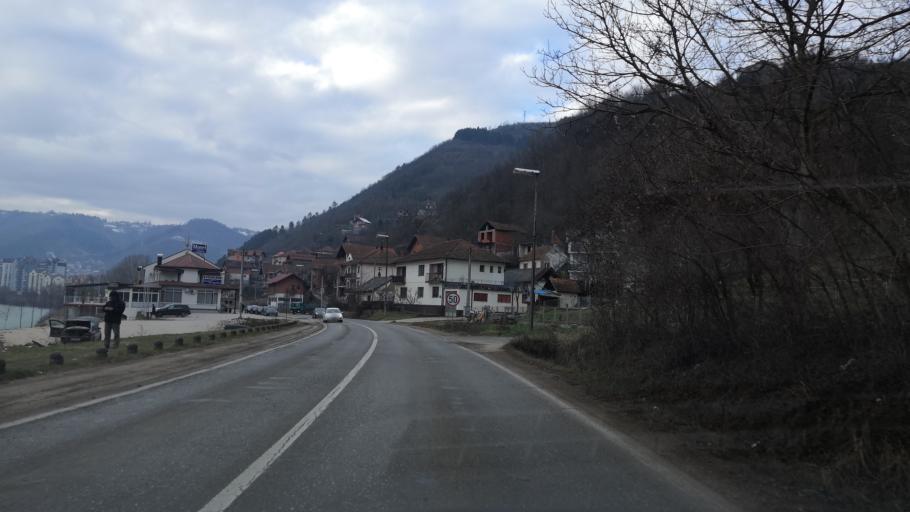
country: BA
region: Republika Srpska
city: Zvornik
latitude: 44.3979
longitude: 19.1092
